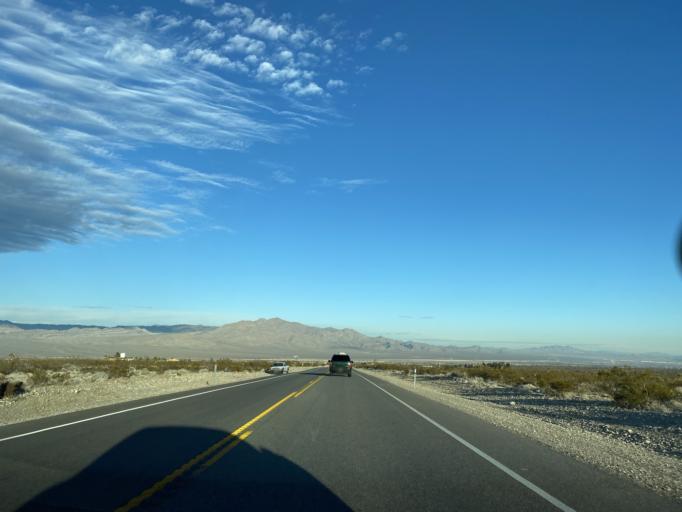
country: US
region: Nevada
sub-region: Clark County
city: Summerlin South
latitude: 36.3097
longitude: -115.3918
